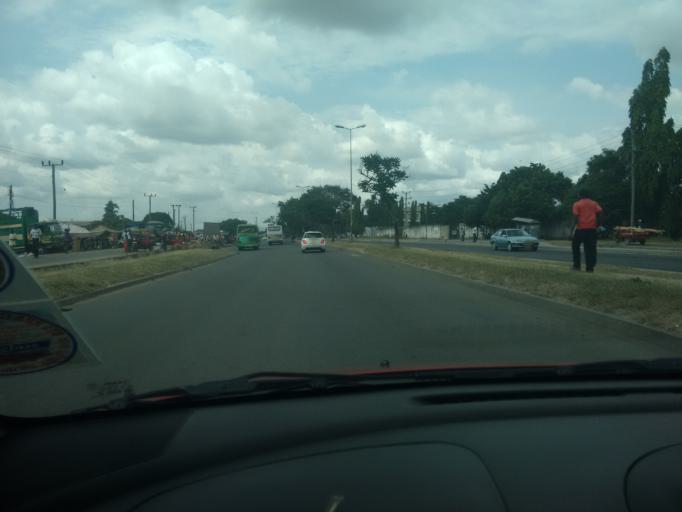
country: TZ
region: Dar es Salaam
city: Dar es Salaam
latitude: -6.8468
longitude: 39.2476
